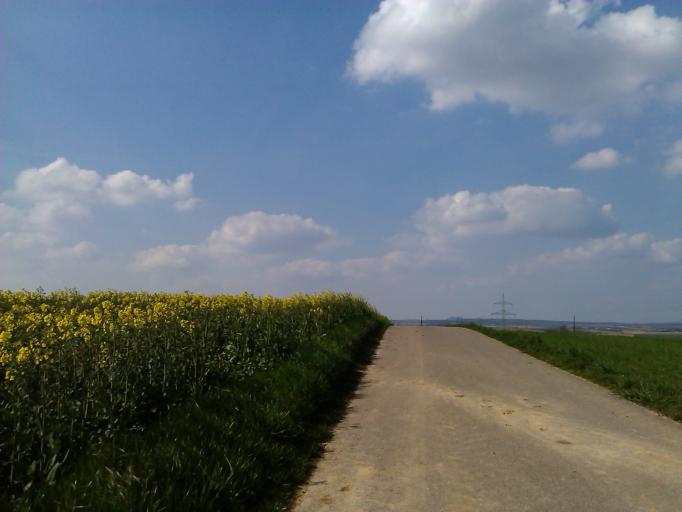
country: DE
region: Baden-Wuerttemberg
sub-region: Regierungsbezirk Stuttgart
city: Eppingen
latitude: 49.1392
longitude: 8.9401
